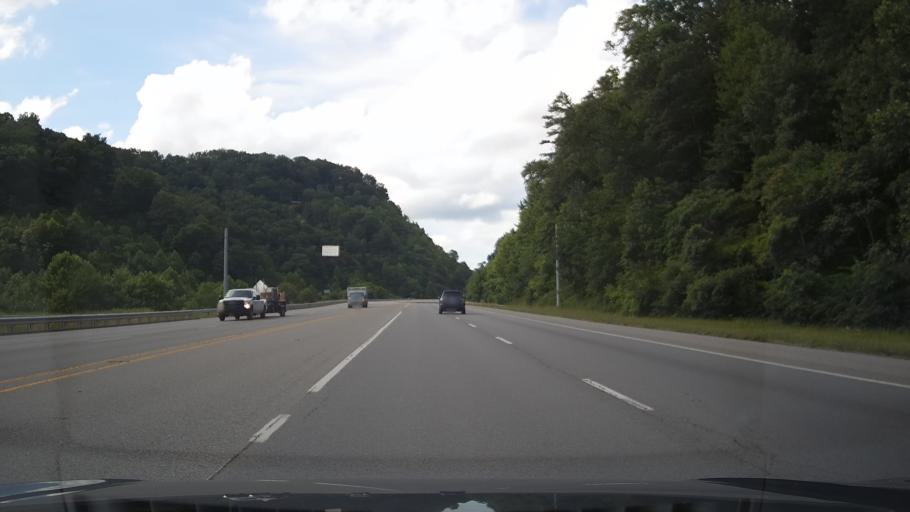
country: US
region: Kentucky
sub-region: Floyd County
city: Prestonsburg
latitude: 37.6885
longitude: -82.7905
